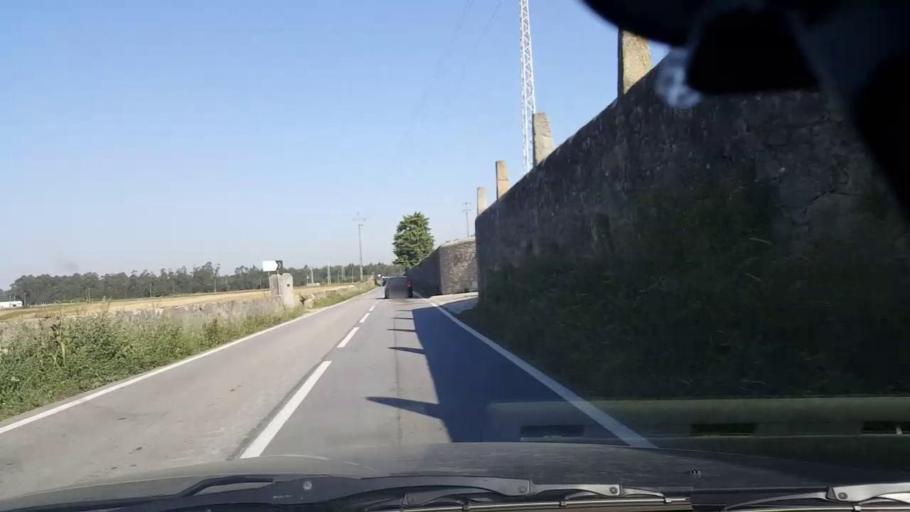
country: PT
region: Porto
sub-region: Vila do Conde
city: Arvore
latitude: 41.3227
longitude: -8.6805
